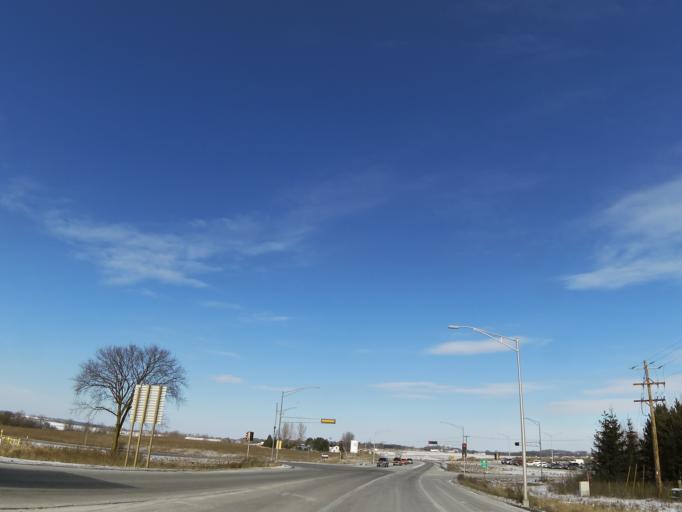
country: US
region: Wisconsin
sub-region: Saint Croix County
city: Roberts
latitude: 44.9627
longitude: -92.5593
